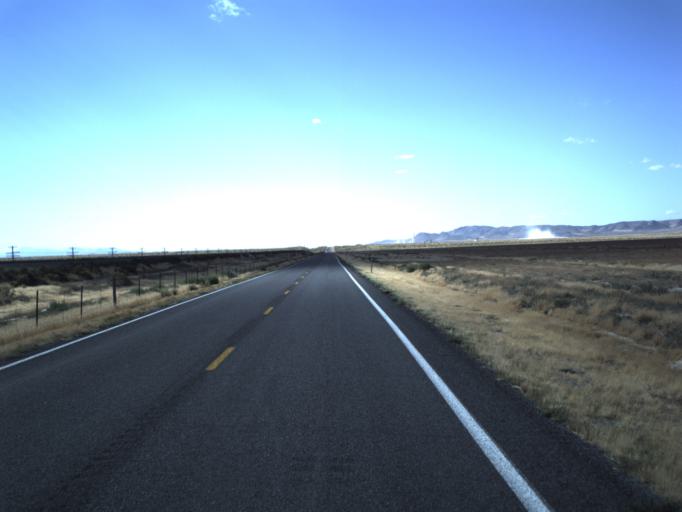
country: US
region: Utah
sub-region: Millard County
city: Delta
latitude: 38.9745
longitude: -112.7977
